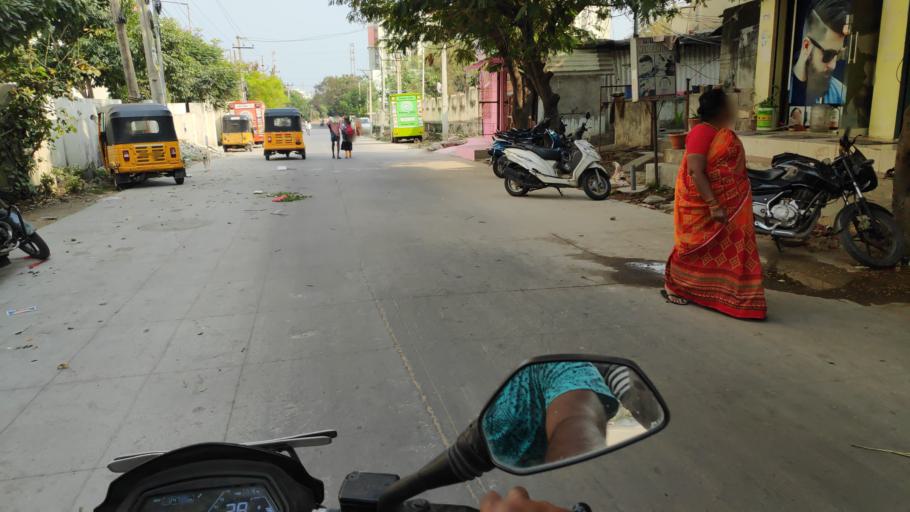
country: IN
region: Telangana
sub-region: Rangareddi
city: Kukatpalli
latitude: 17.4711
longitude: 78.3908
